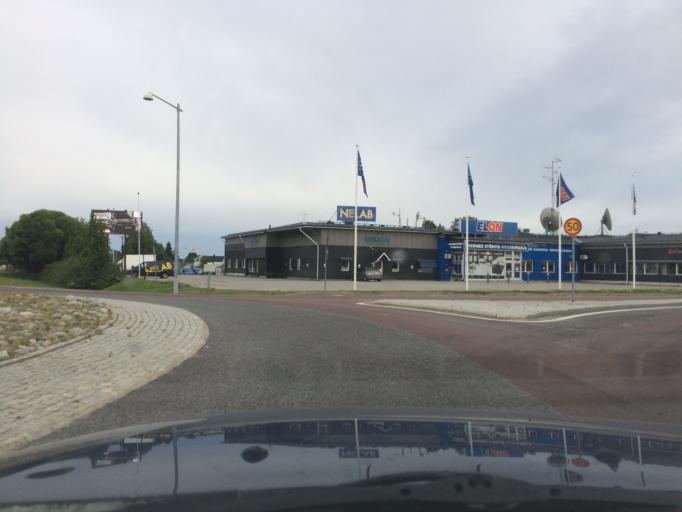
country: SE
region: Norrbotten
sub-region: Pitea Kommun
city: Pitea
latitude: 65.3239
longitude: 21.4486
